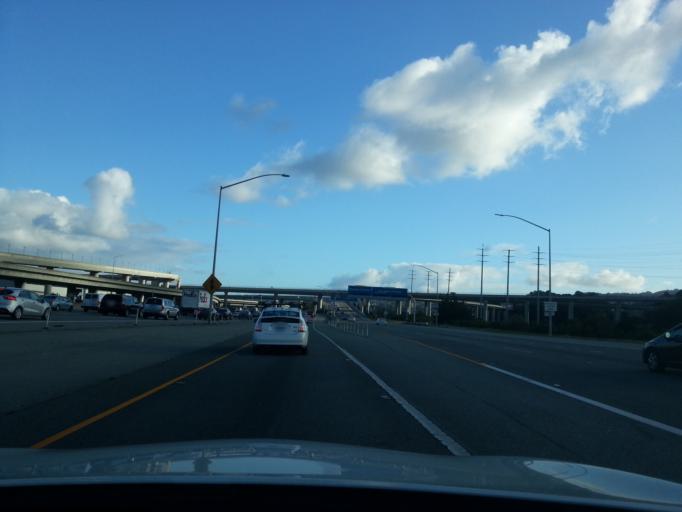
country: US
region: California
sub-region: San Mateo County
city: San Bruno
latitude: 37.6190
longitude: -122.3997
